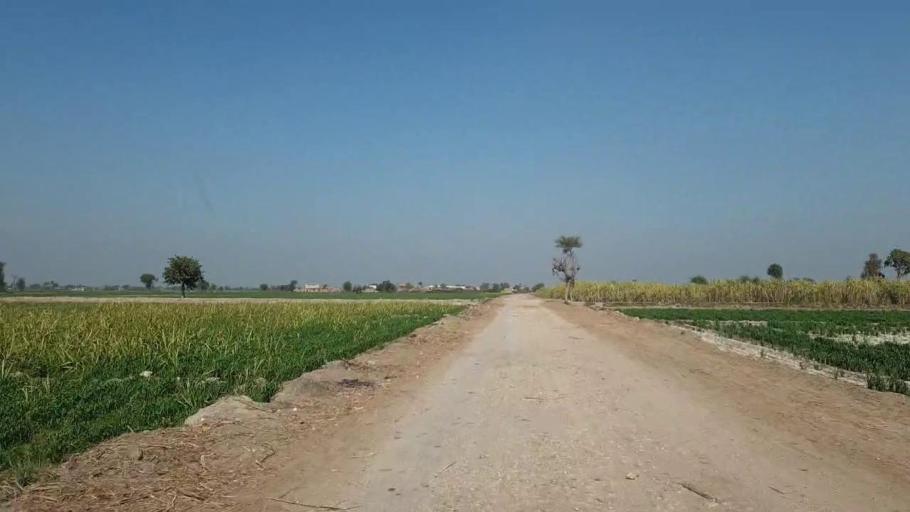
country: PK
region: Sindh
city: Shahdadpur
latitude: 25.9472
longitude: 68.5111
